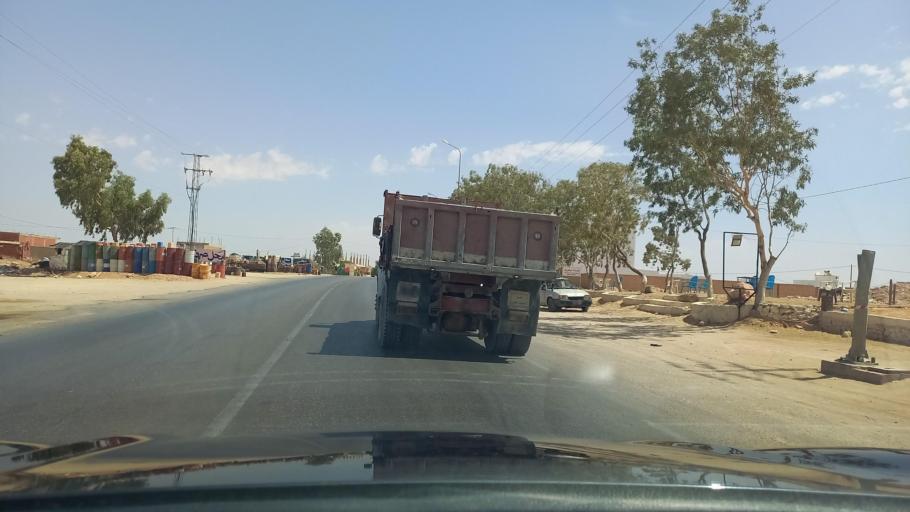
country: TN
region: Madanin
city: Medenine
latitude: 33.3671
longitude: 10.4548
